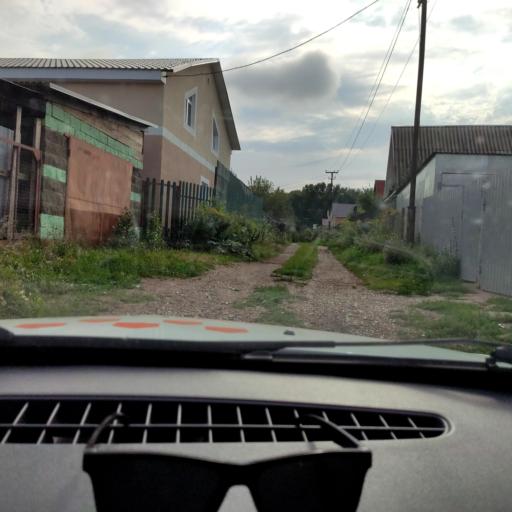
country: RU
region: Bashkortostan
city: Ufa
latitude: 54.5975
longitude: 55.8979
